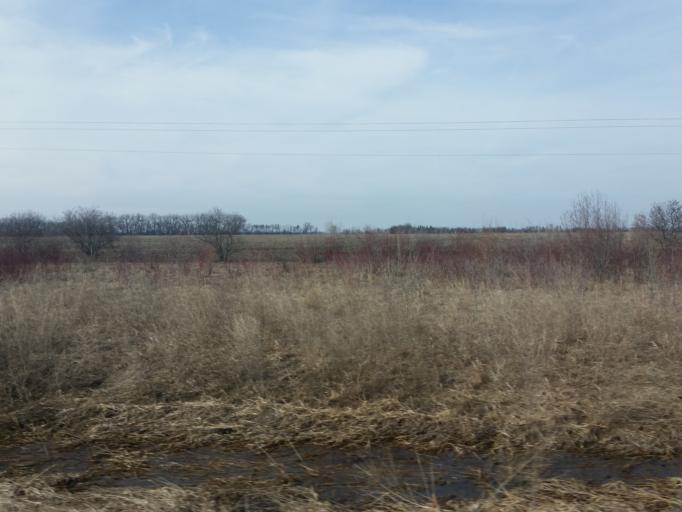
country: US
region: Minnesota
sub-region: Wilkin County
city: Breckenridge
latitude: 46.4712
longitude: -96.5476
